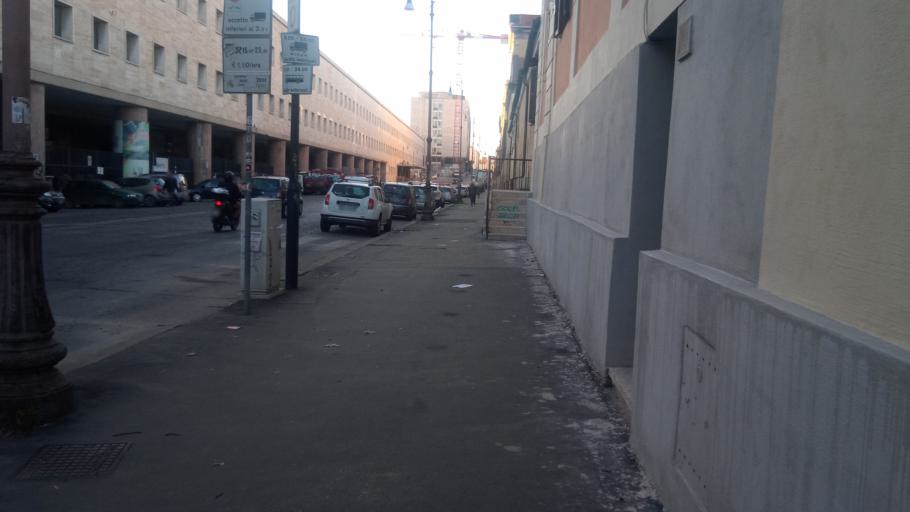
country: IT
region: Latium
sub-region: Citta metropolitana di Roma Capitale
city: Rome
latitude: 41.8985
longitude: 12.5089
